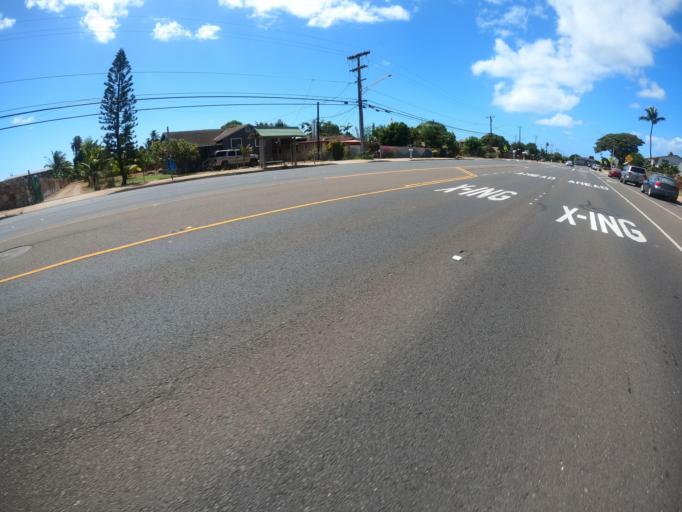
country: US
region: Hawaii
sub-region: Honolulu County
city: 'Ewa Beach
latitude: 21.3120
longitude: -158.0063
